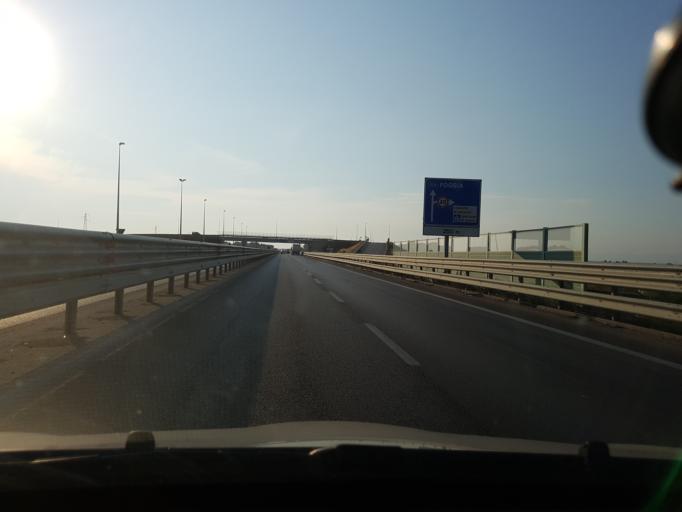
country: IT
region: Apulia
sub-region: Provincia di Foggia
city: Stornara
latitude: 41.3187
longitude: 15.7870
